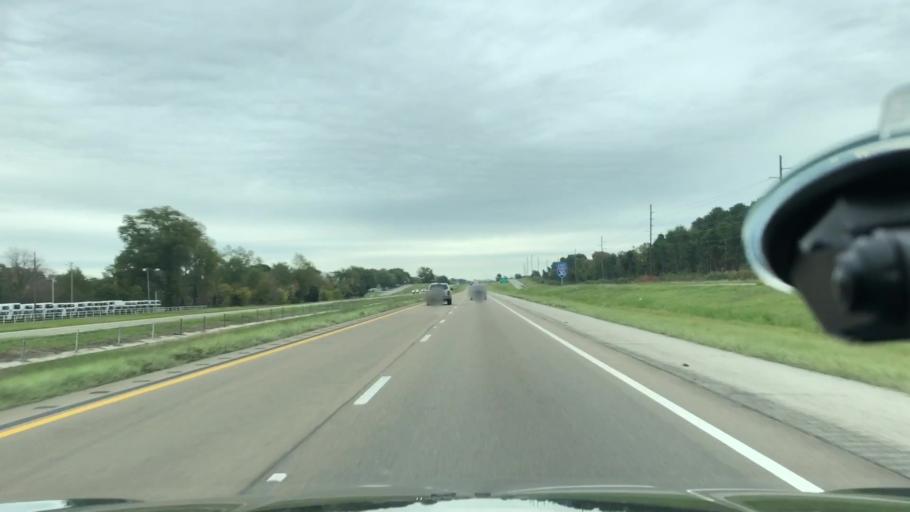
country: US
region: Texas
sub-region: Titus County
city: Mount Pleasant
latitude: 33.1590
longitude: -95.0648
